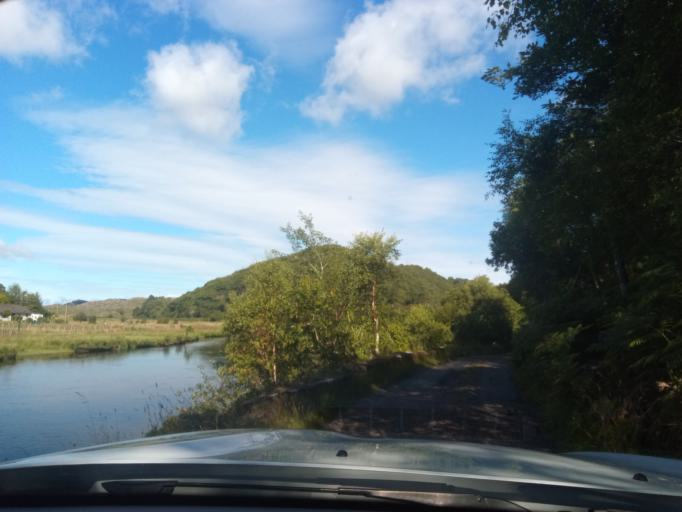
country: GB
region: Scotland
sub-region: Argyll and Bute
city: Isle Of Mull
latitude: 56.7638
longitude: -5.8202
